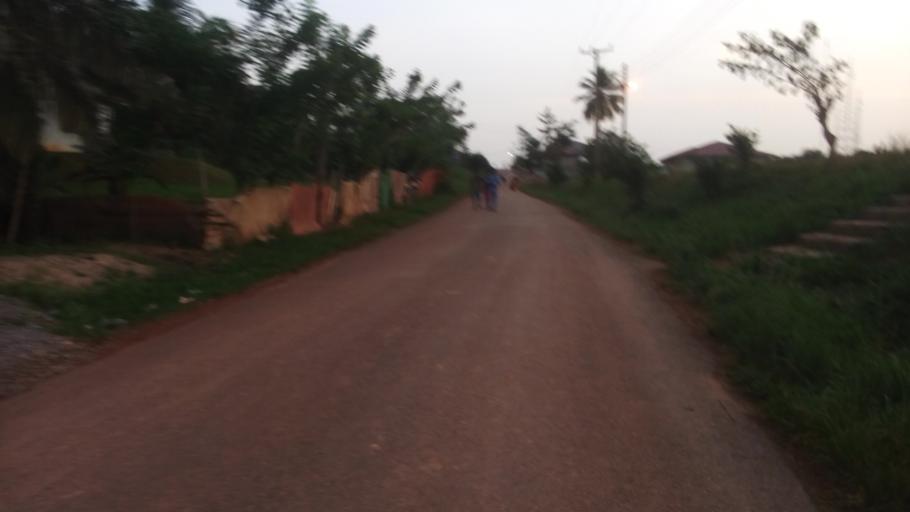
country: GH
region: Western
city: Tarkwa
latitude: 5.3079
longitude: -2.0002
